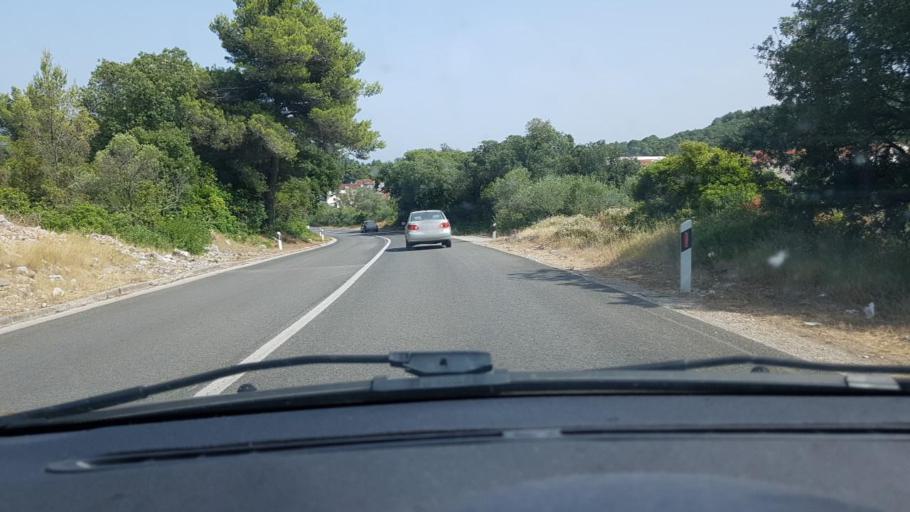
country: HR
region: Dubrovacko-Neretvanska
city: Korcula
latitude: 42.9490
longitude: 17.1317
